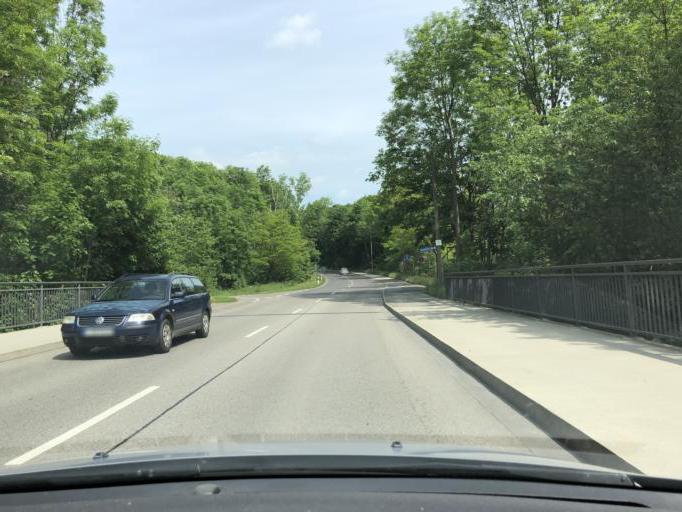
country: DE
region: Thuringia
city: Altenburg
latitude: 51.0025
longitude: 12.4430
